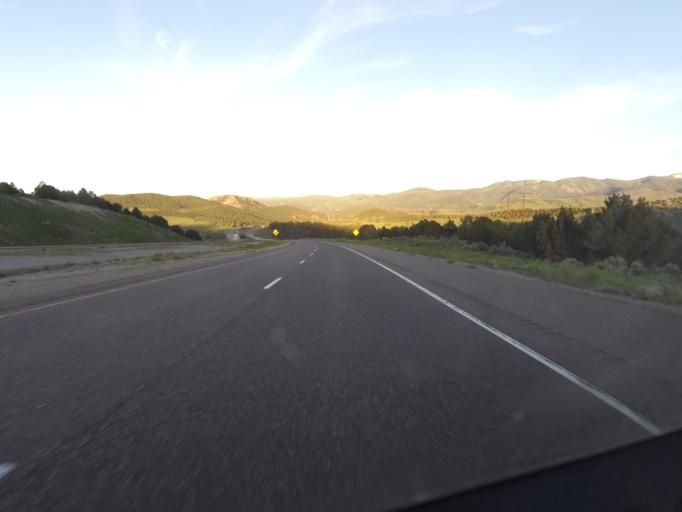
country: US
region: Utah
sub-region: Beaver County
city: Beaver
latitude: 38.5751
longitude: -112.4690
